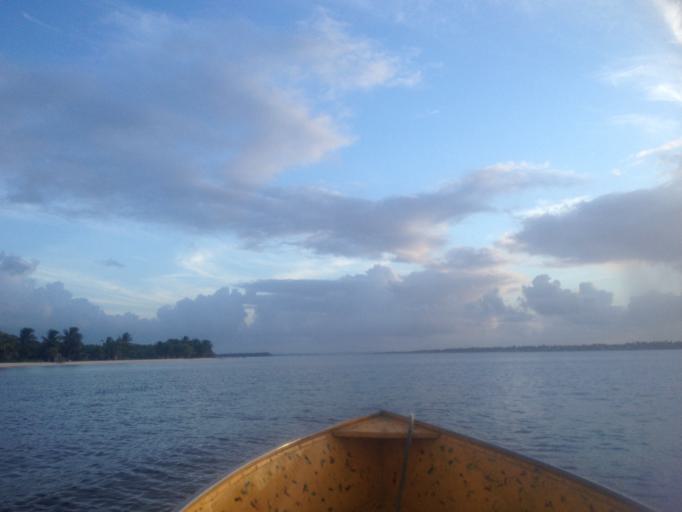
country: BR
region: Sergipe
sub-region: Indiaroba
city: Indiaroba
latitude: -11.4729
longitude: -37.3800
